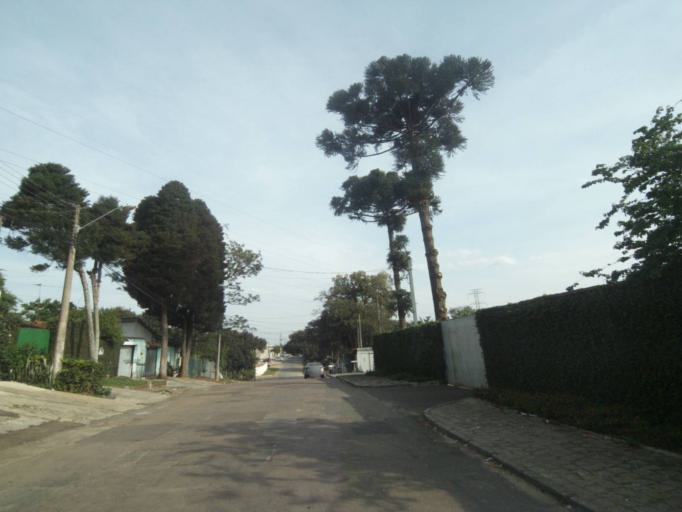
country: BR
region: Parana
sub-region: Curitiba
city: Curitiba
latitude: -25.4636
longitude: -49.3142
